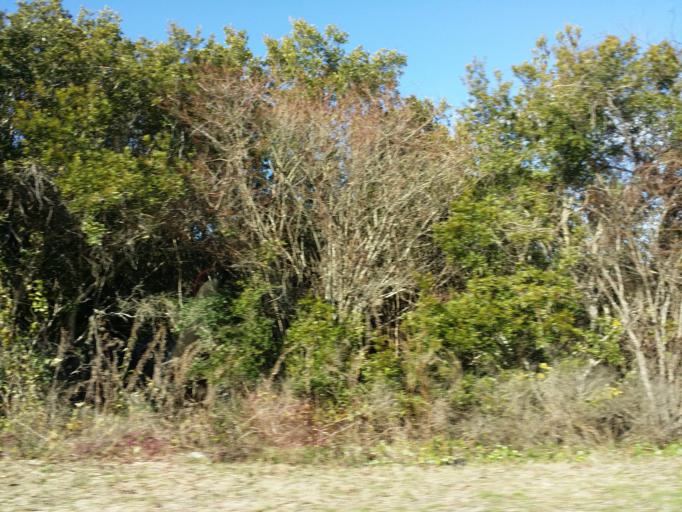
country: US
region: North Carolina
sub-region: Pender County
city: Surf City
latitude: 34.4528
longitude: -77.5008
